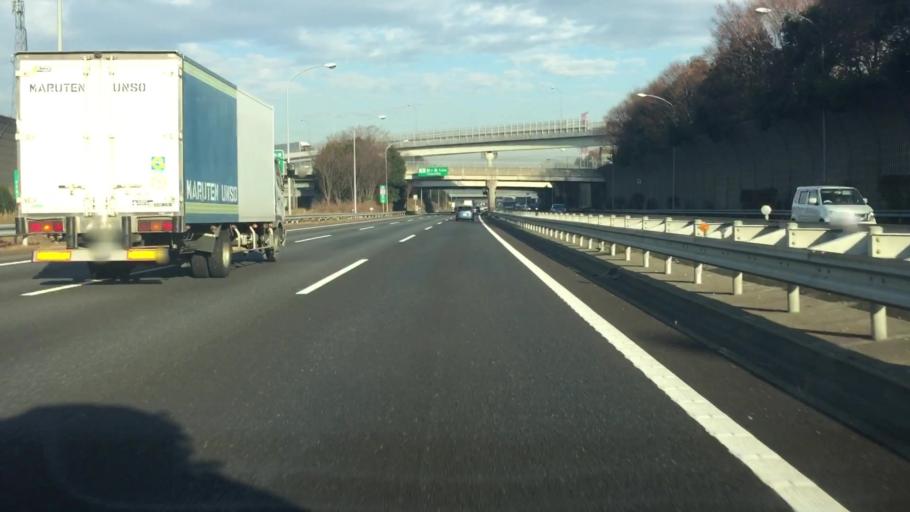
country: JP
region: Saitama
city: Sakado
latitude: 35.9303
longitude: 139.4082
